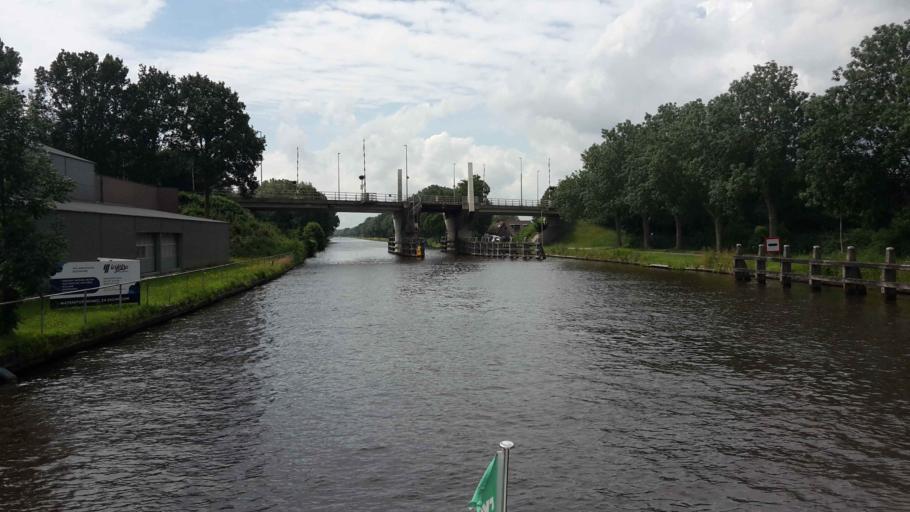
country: NL
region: Overijssel
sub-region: Gemeente Steenwijkerland
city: Tuk
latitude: 52.7741
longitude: 6.0871
